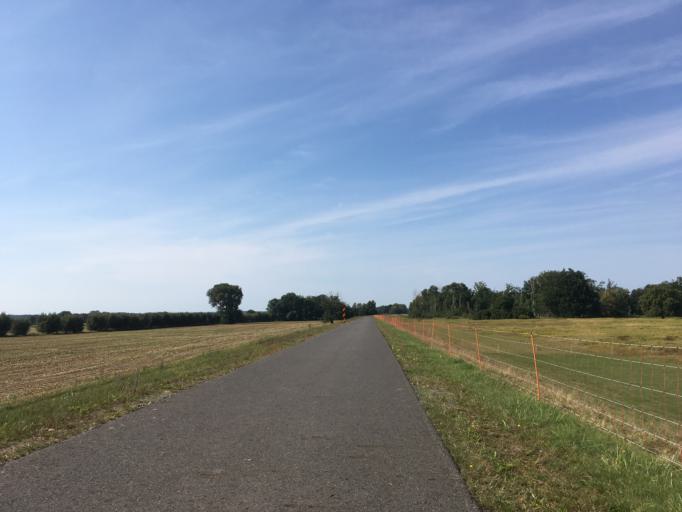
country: DE
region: Brandenburg
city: Neuzelle
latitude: 52.0857
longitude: 14.7326
